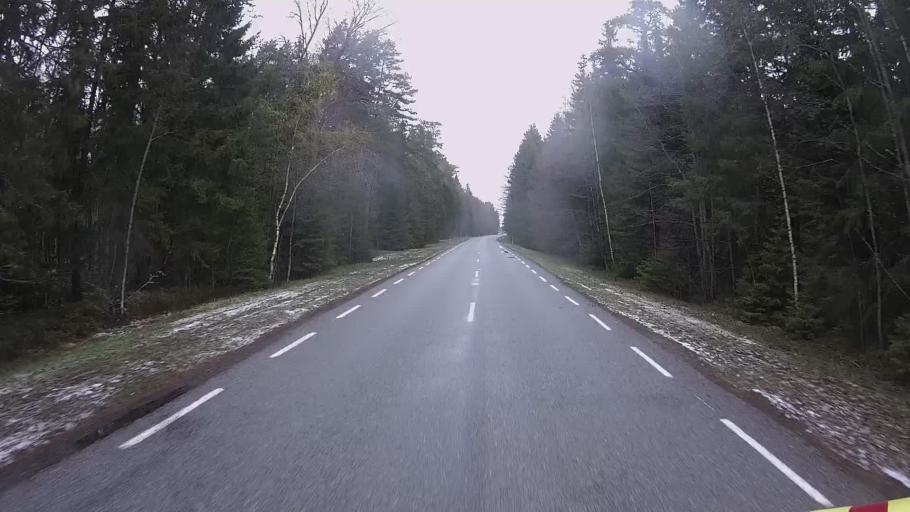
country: EE
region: Hiiumaa
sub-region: Kaerdla linn
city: Kardla
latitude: 59.0575
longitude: 22.6831
